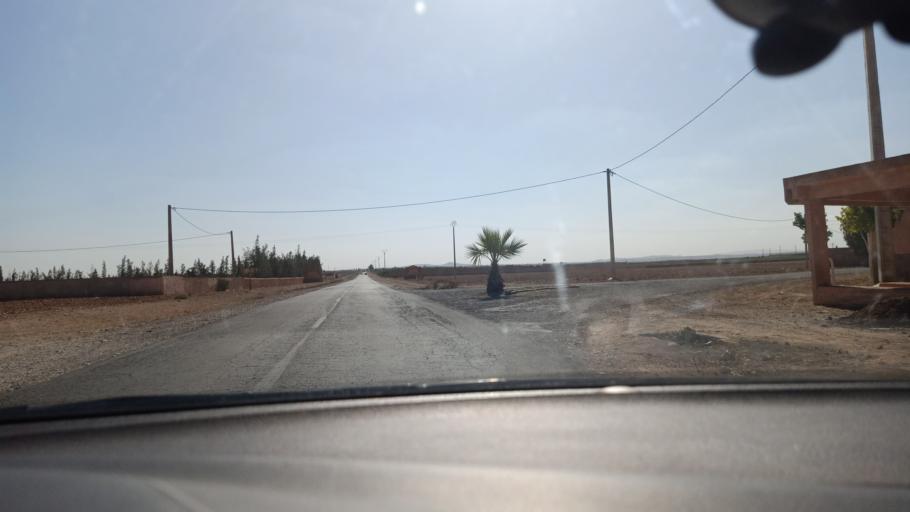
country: MA
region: Doukkala-Abda
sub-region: Safi
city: Youssoufia
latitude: 32.1312
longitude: -8.5992
